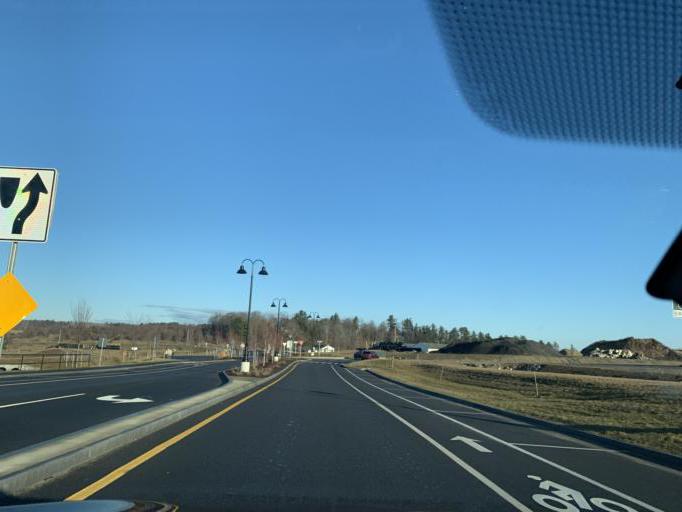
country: US
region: New Hampshire
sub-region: Rockingham County
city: Derry
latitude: 42.8732
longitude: -71.3503
